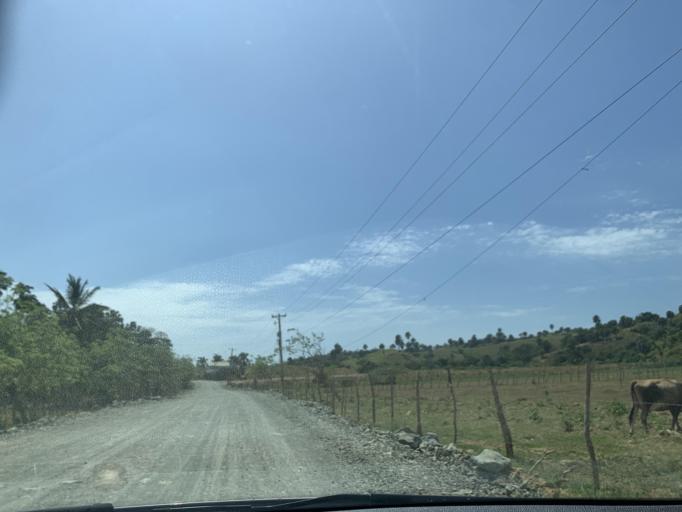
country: DO
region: Puerto Plata
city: Luperon
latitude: 19.8822
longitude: -70.8443
